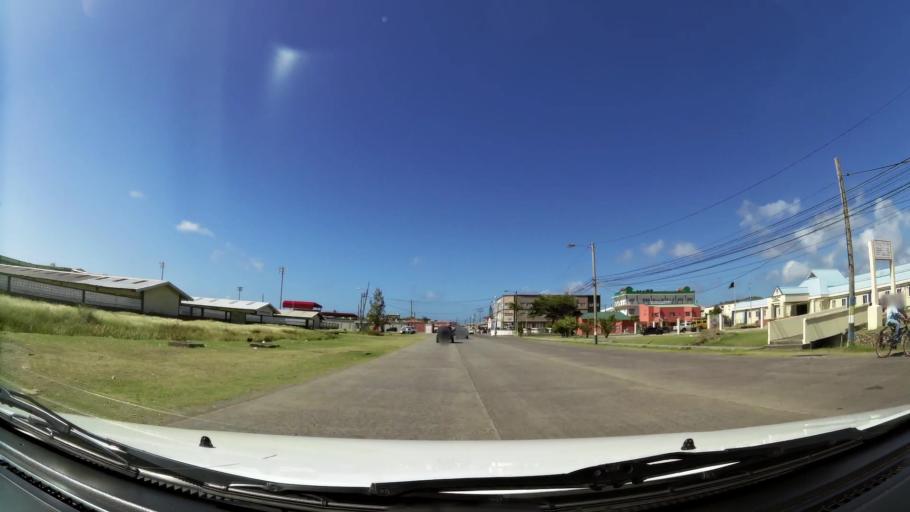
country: LC
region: Vieux-Fort
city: Vieux Fort
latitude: 13.7298
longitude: -60.9491
